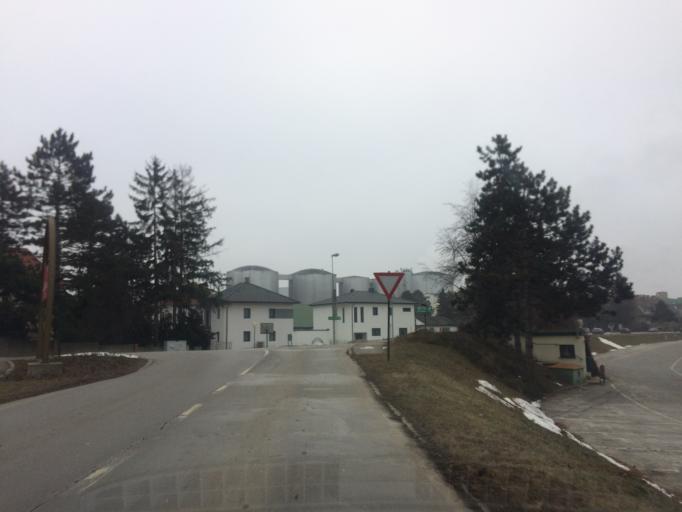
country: AT
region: Lower Austria
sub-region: Politischer Bezirk Tulln
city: Tulln
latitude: 48.3283
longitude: 16.0438
